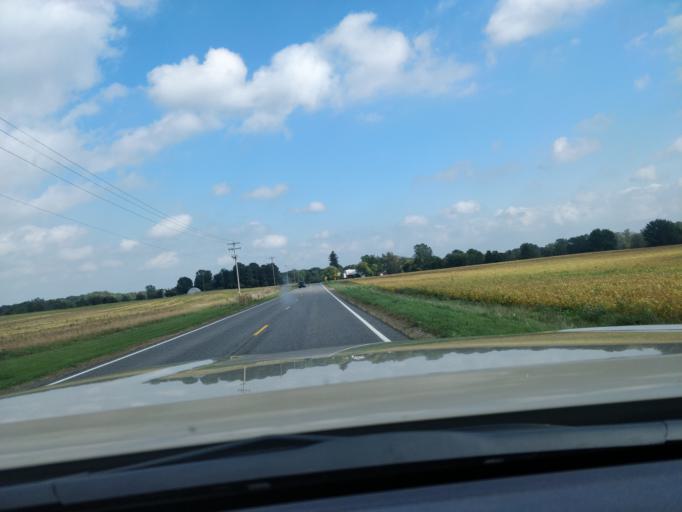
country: US
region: Michigan
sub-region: Ionia County
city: Saranac
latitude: 42.8861
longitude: -85.2207
